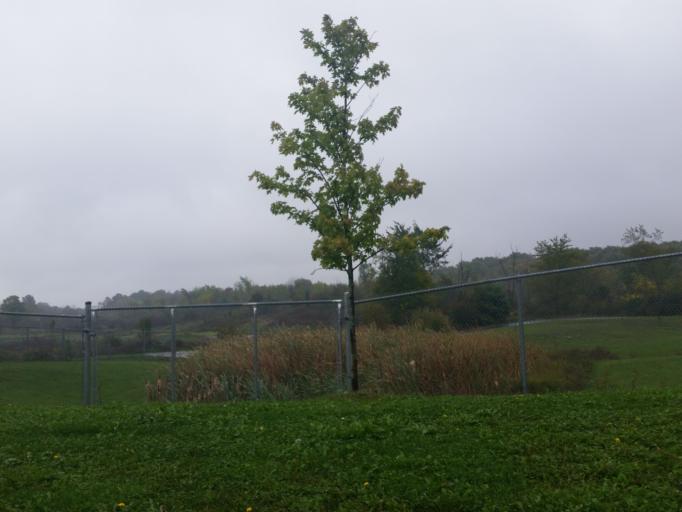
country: CA
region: Ontario
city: Kingston
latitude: 44.2653
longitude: -76.4424
